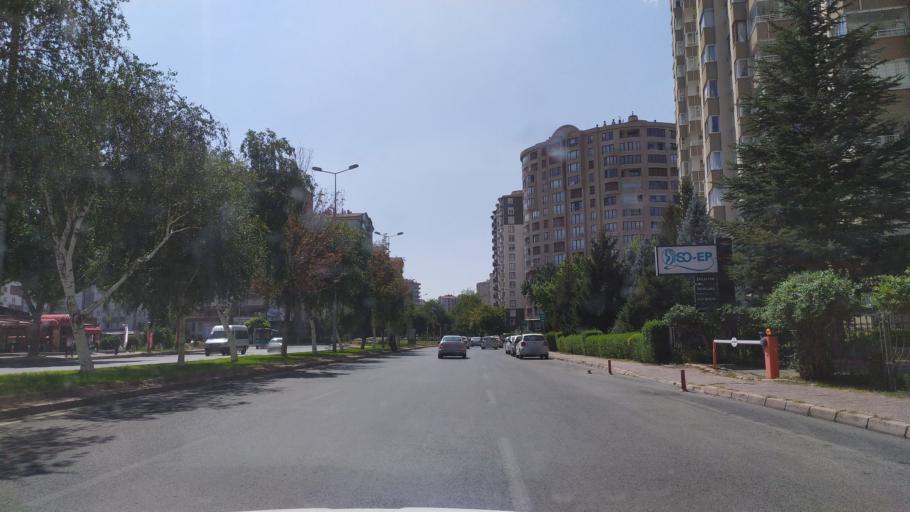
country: TR
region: Kayseri
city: Kayseri
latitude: 38.7259
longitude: 35.5215
